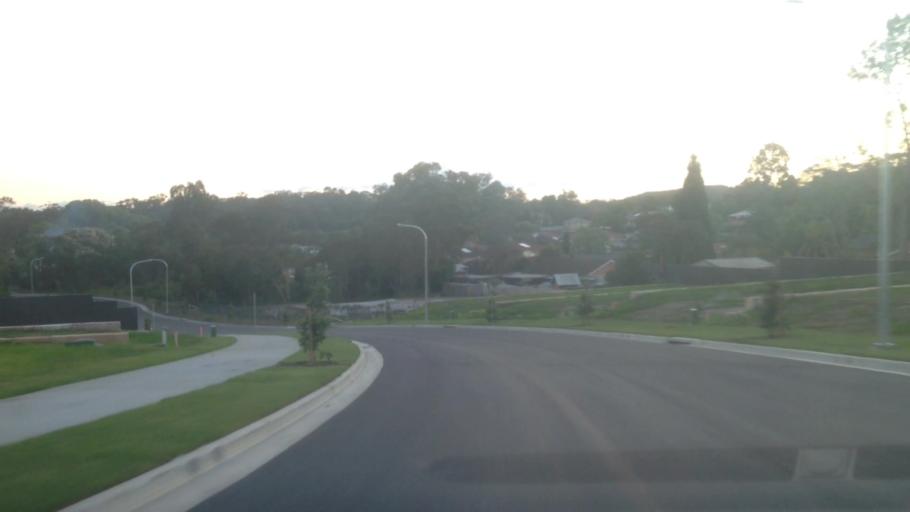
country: AU
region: New South Wales
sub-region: Lake Macquarie Shire
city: Cooranbong
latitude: -33.0711
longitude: 151.4569
